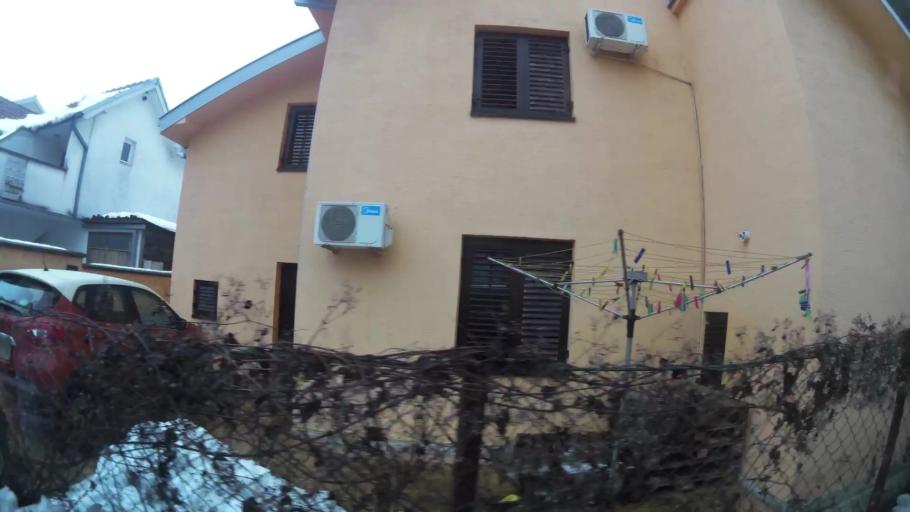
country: RS
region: Central Serbia
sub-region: Belgrade
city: Zvezdara
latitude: 44.7835
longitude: 20.5248
